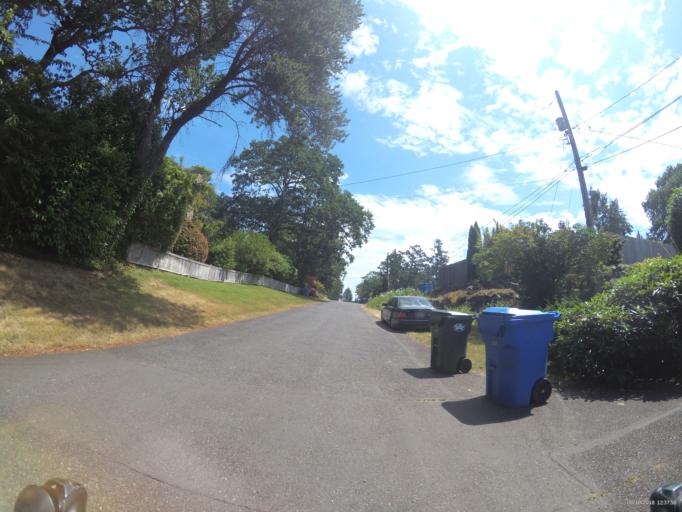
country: US
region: Washington
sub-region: Pierce County
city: Lakewood
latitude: 47.1667
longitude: -122.5296
